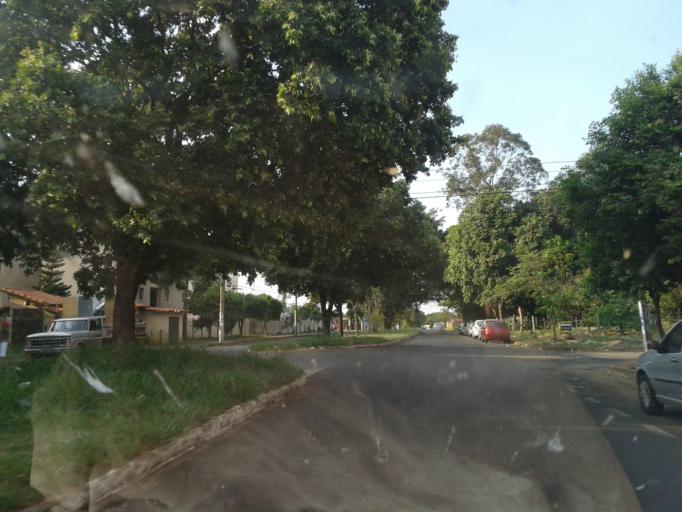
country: BR
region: Minas Gerais
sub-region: Uberlandia
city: Uberlandia
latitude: -18.9356
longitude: -48.3208
